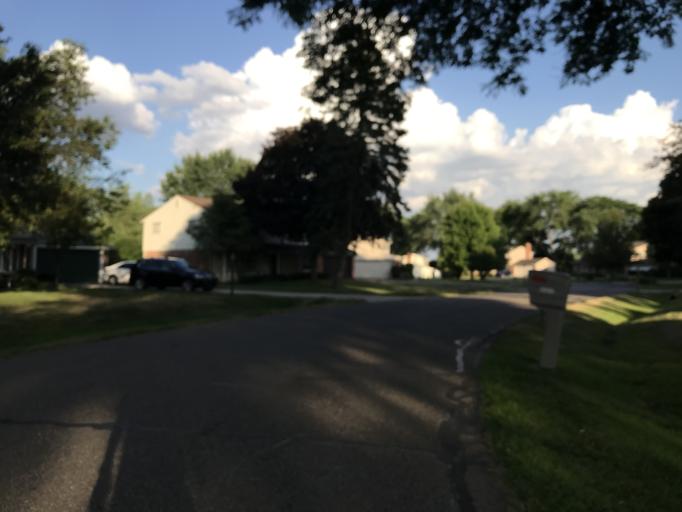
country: US
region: Michigan
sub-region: Oakland County
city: Farmington Hills
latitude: 42.4871
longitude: -83.3411
